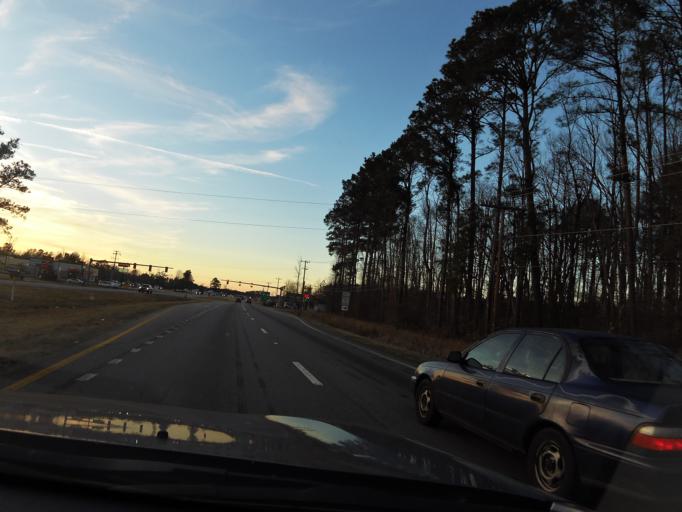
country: US
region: Virginia
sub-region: Southampton County
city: Courtland
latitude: 36.6860
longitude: -77.0215
